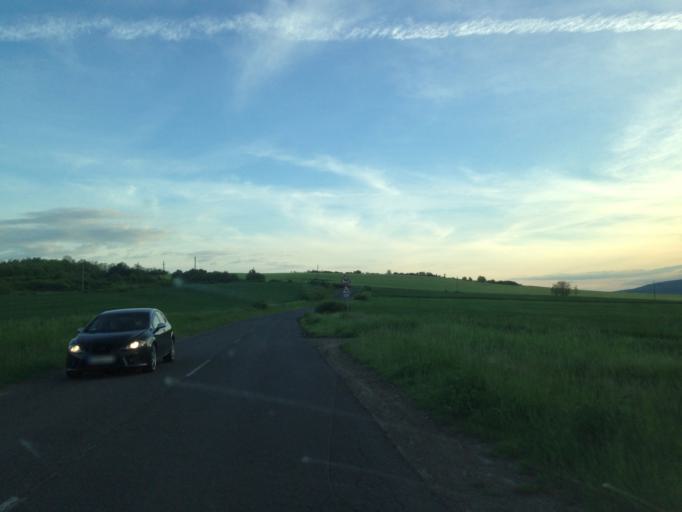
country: HU
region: Nograd
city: Tar
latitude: 47.9439
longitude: 19.7276
